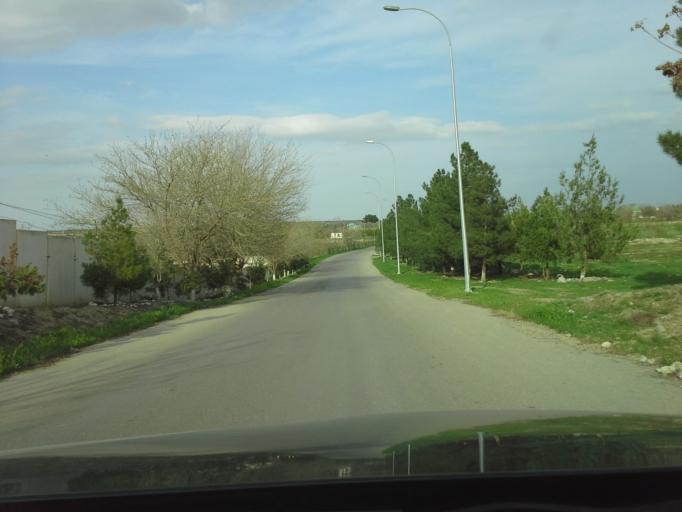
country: TM
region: Ahal
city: Abadan
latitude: 37.9323
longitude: 58.2214
